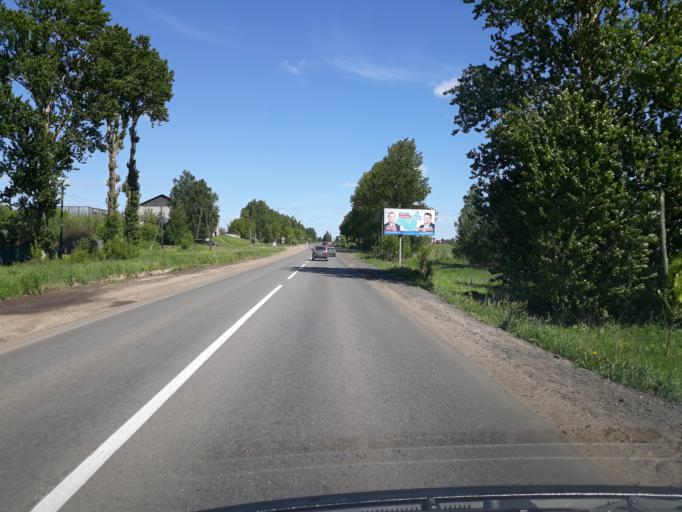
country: RU
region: Jaroslavl
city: Yaroslavl
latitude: 57.6688
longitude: 40.0148
